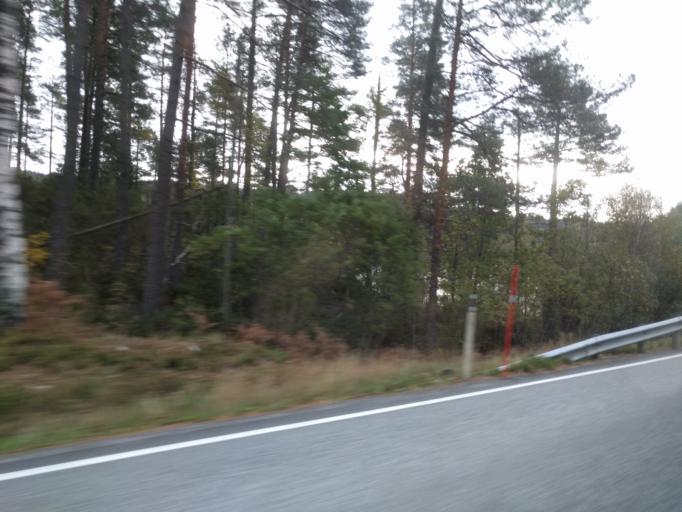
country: NO
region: Aust-Agder
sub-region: Iveland
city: Birketveit
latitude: 58.3445
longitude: 7.8078
